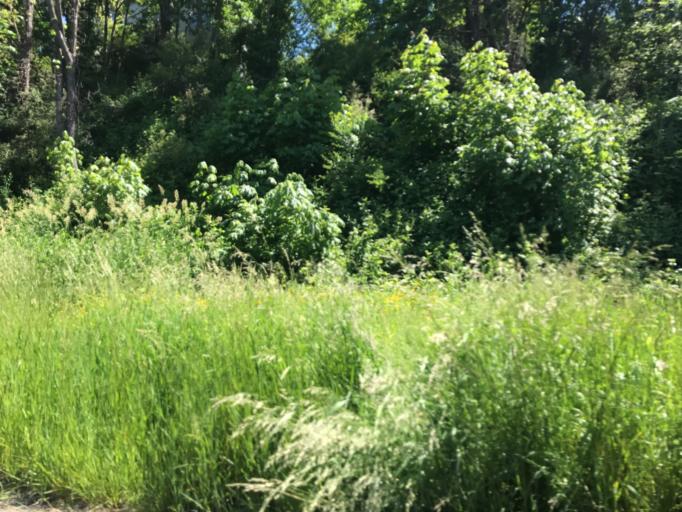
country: US
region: Washington
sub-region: King County
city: Seattle
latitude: 47.5859
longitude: -122.2964
